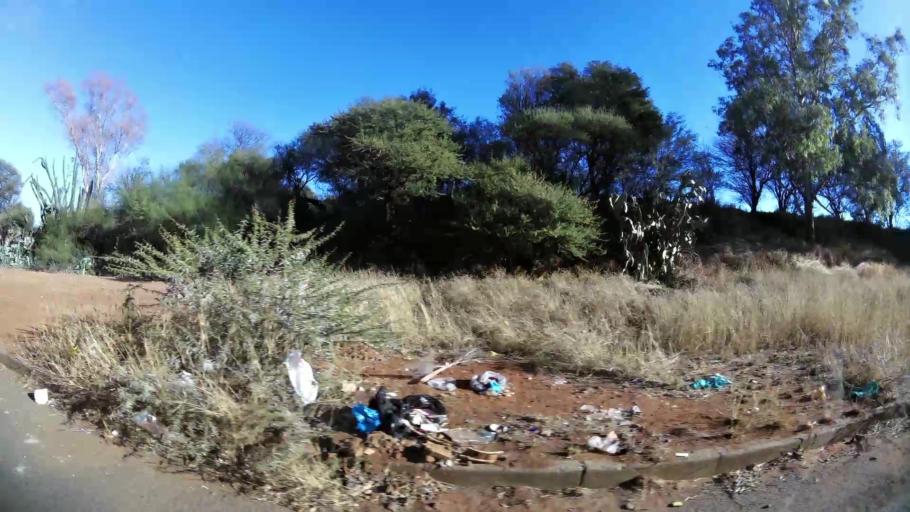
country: ZA
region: Northern Cape
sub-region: Frances Baard District Municipality
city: Kimberley
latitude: -28.7566
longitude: 24.7766
